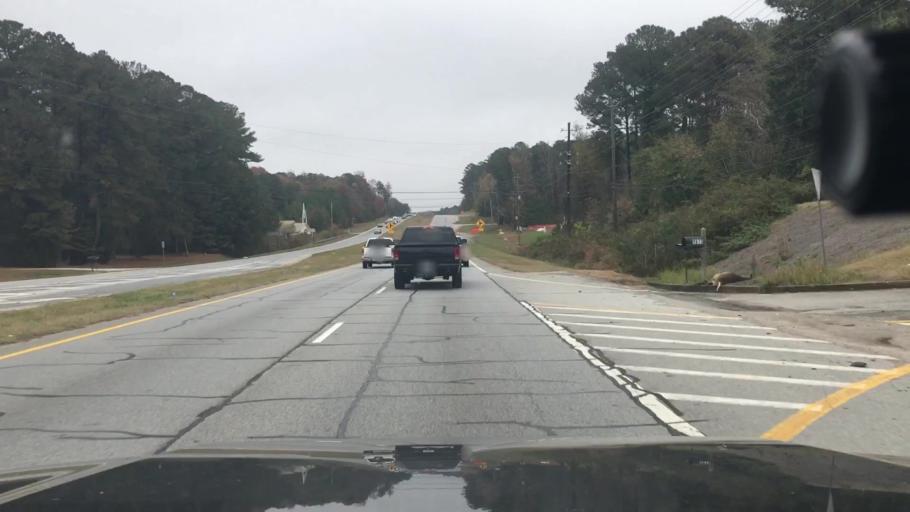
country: US
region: Georgia
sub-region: Coweta County
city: East Newnan
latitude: 33.4034
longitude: -84.7162
